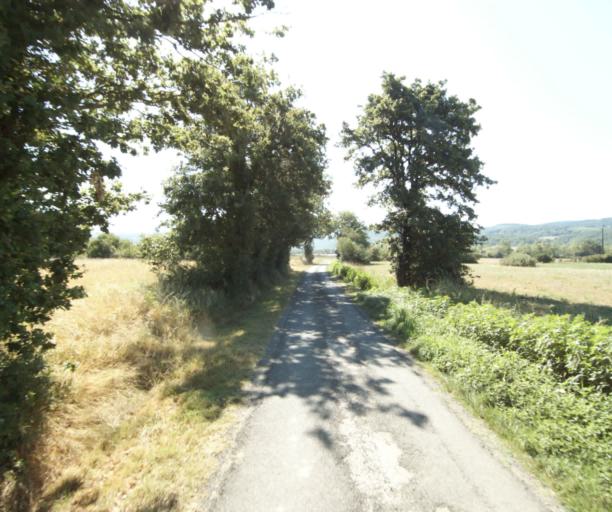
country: FR
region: Midi-Pyrenees
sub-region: Departement de la Haute-Garonne
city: Revel
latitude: 43.4578
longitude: 2.0324
